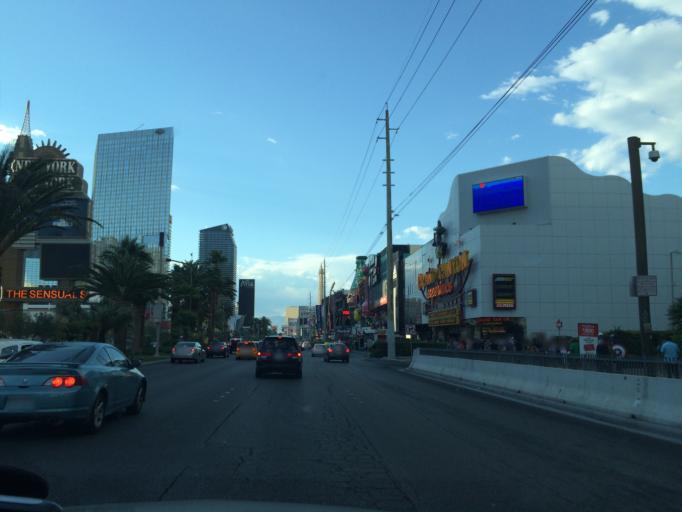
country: US
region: Nevada
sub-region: Clark County
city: Paradise
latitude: 36.1018
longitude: -115.1728
